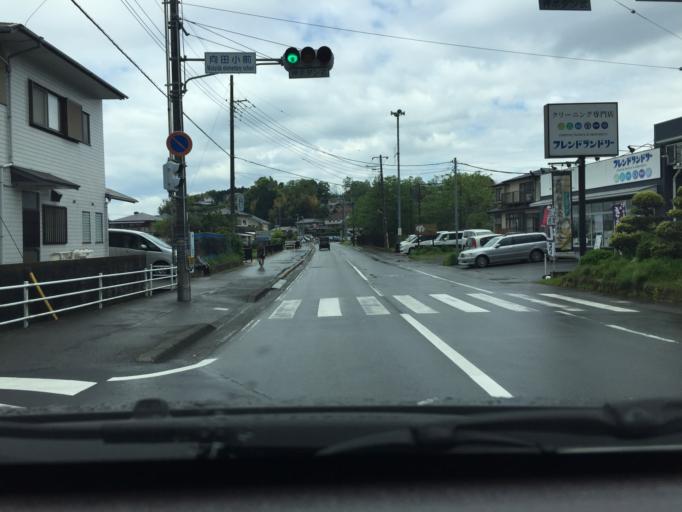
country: JP
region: Shizuoka
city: Mishima
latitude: 35.1730
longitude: 138.9224
